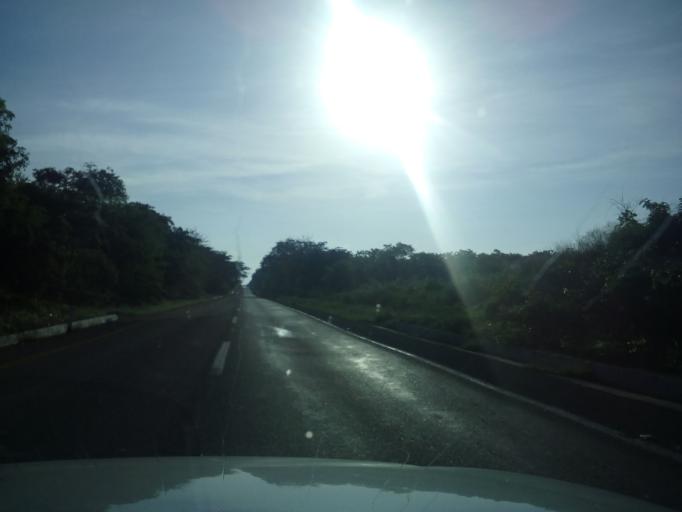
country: MX
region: Yucatan
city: Chichen-Itza
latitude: 20.7110
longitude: -88.4791
